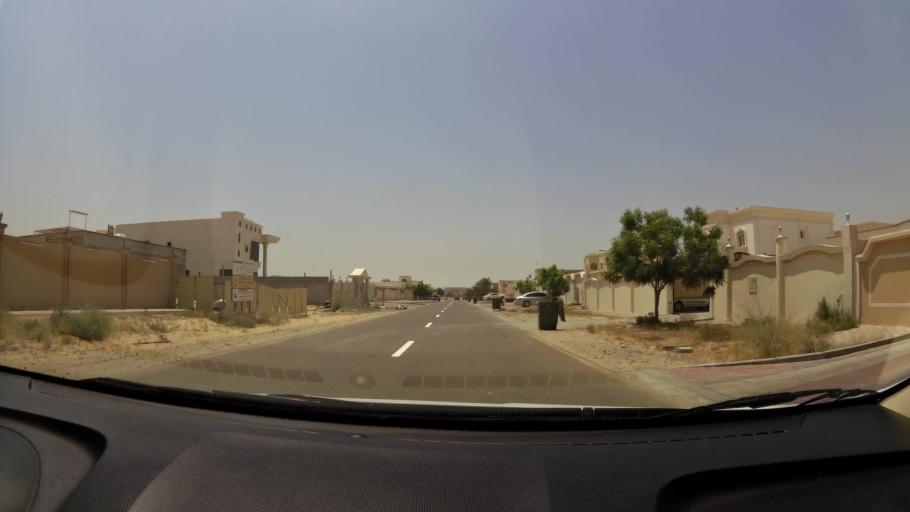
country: AE
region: Ajman
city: Ajman
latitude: 25.4273
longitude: 55.5162
